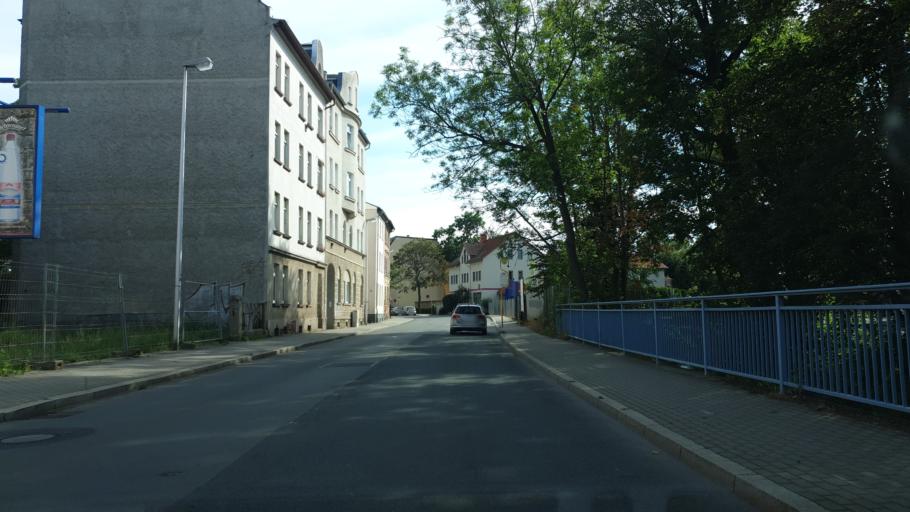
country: DE
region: Thuringia
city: Gera
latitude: 50.8606
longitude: 12.0828
